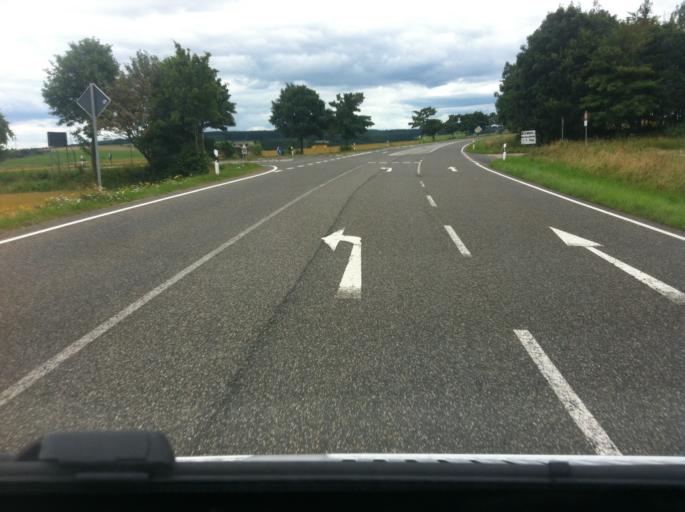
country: DE
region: North Rhine-Westphalia
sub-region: Regierungsbezirk Koln
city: Nettersheim
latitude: 50.4900
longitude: 6.6172
